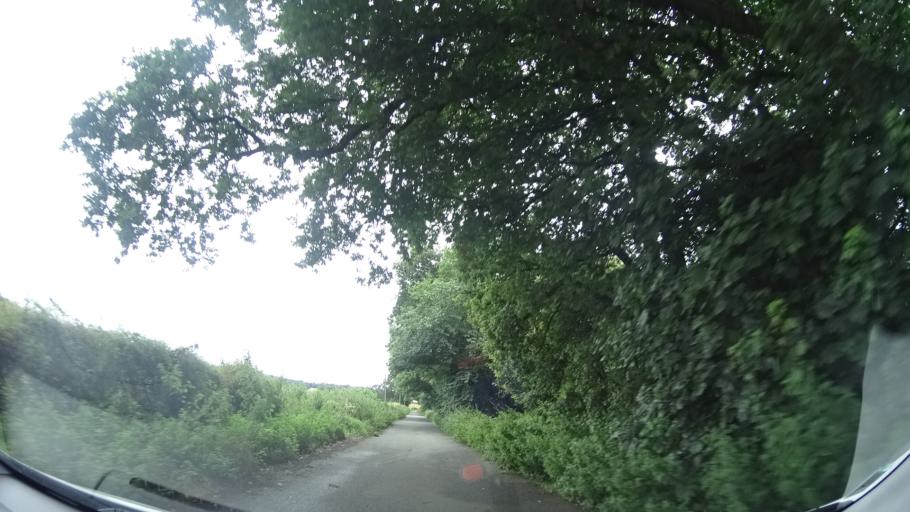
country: GB
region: Scotland
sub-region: West Lothian
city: Kirknewton
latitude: 55.9177
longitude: -3.4309
